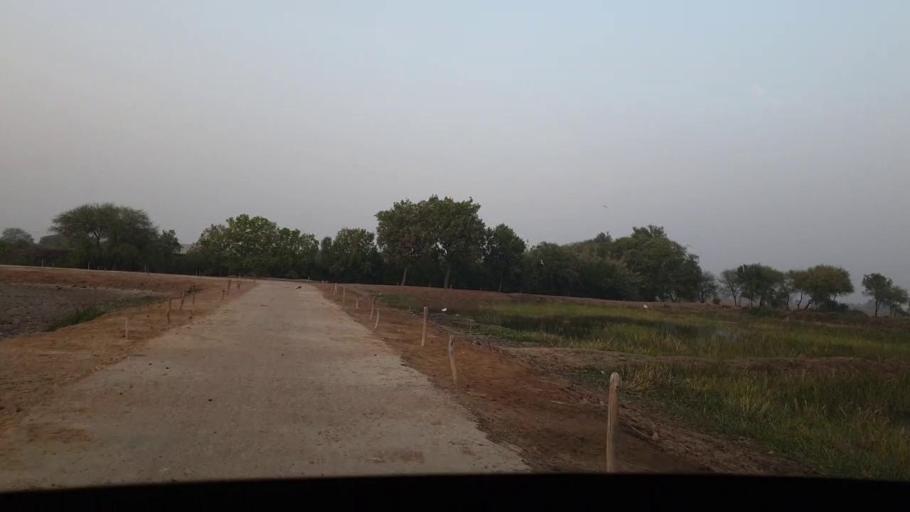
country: PK
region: Sindh
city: Chuhar Jamali
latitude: 24.4640
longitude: 68.0321
